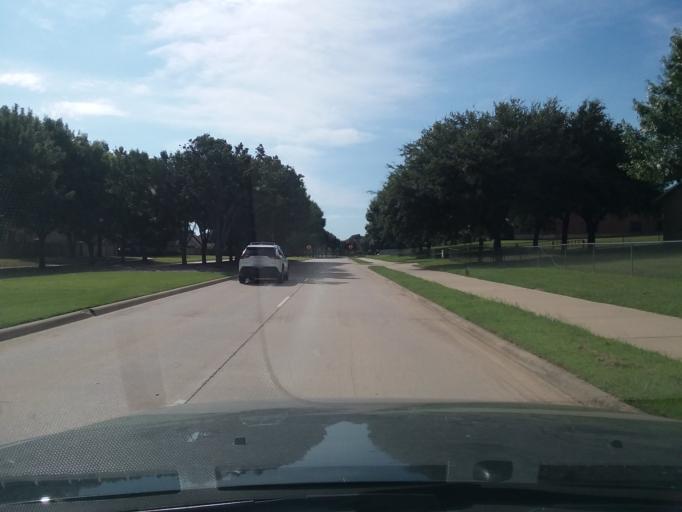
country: US
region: Texas
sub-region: Denton County
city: Flower Mound
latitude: 33.0319
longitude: -97.0928
